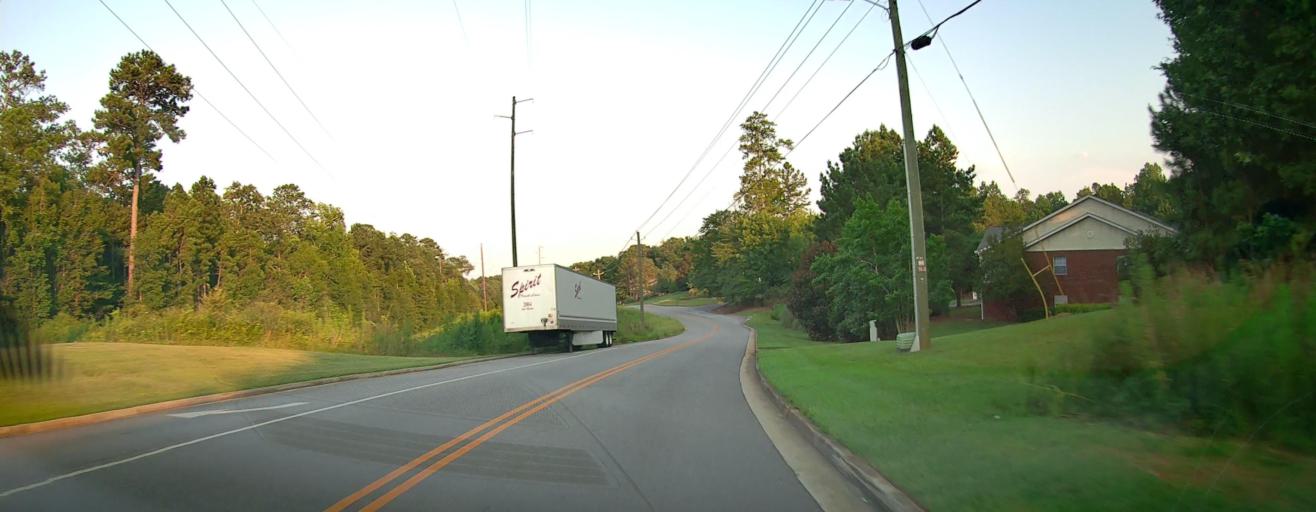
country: US
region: Georgia
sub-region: Bibb County
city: Macon
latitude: 32.9176
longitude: -83.7185
